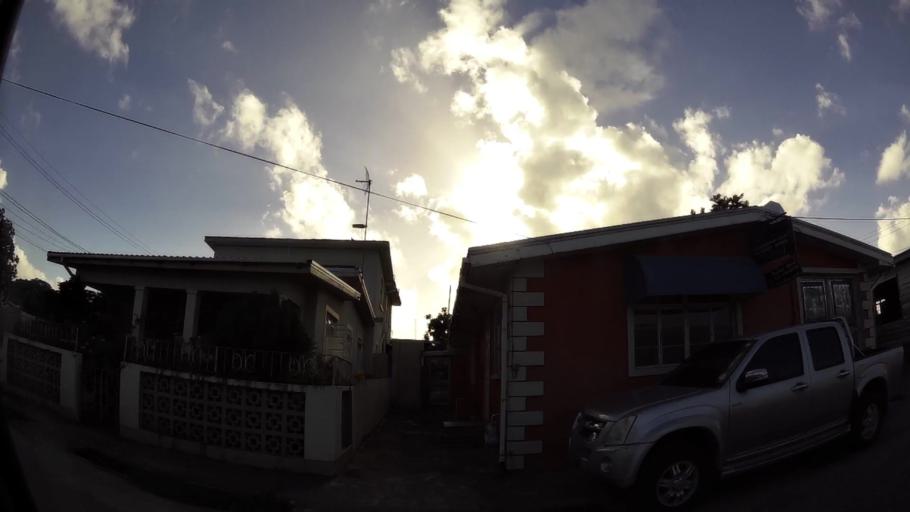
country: BB
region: Saint Michael
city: Bridgetown
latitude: 13.0891
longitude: -59.5939
